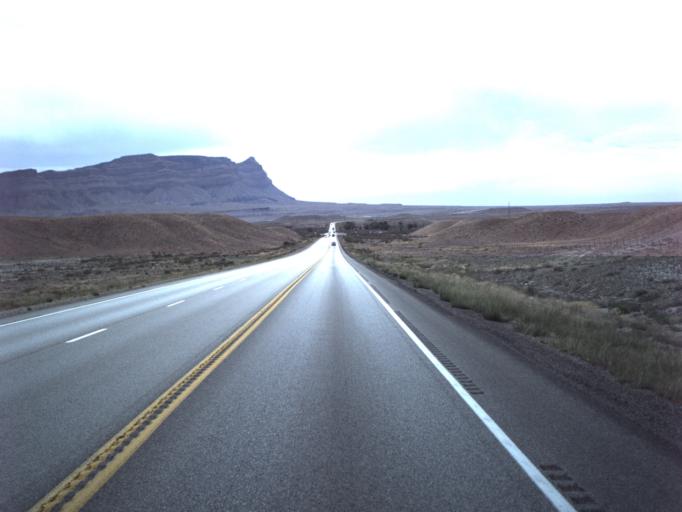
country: US
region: Utah
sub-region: Carbon County
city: East Carbon City
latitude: 39.2761
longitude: -110.3476
